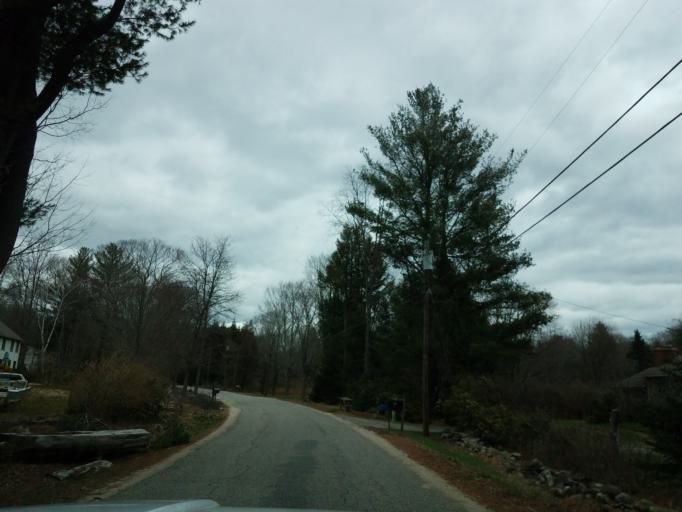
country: US
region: Connecticut
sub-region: Tolland County
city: Coventry Lake
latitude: 41.7628
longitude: -72.3949
